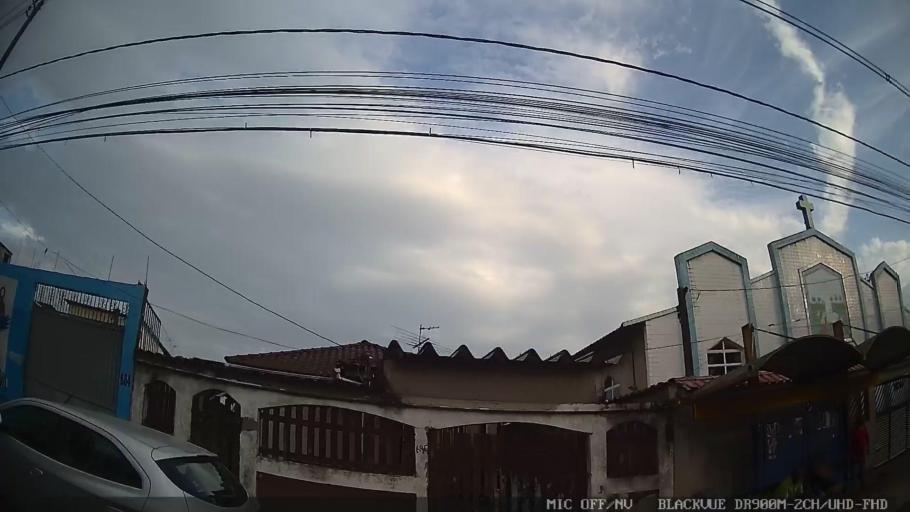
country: BR
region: Sao Paulo
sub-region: Cubatao
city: Cubatao
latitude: -23.8987
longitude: -46.4358
